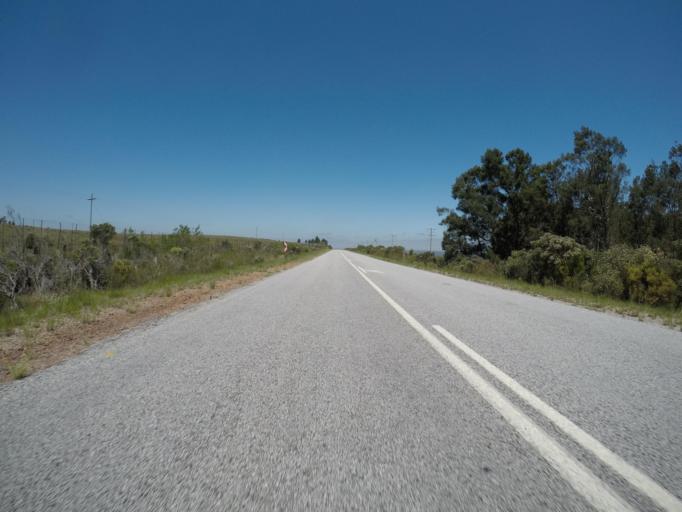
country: ZA
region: Eastern Cape
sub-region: Cacadu District Municipality
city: Kruisfontein
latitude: -33.9932
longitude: 24.5339
